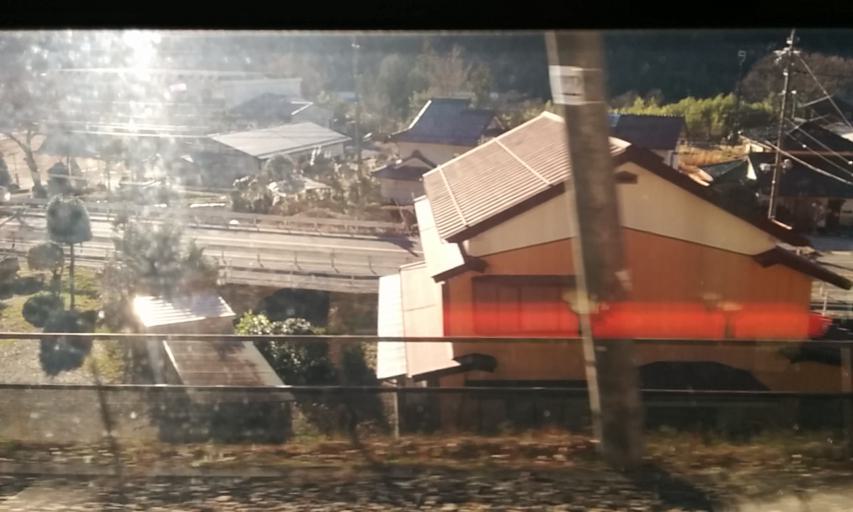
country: JP
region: Nagano
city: Iida
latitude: 35.7428
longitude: 137.7162
